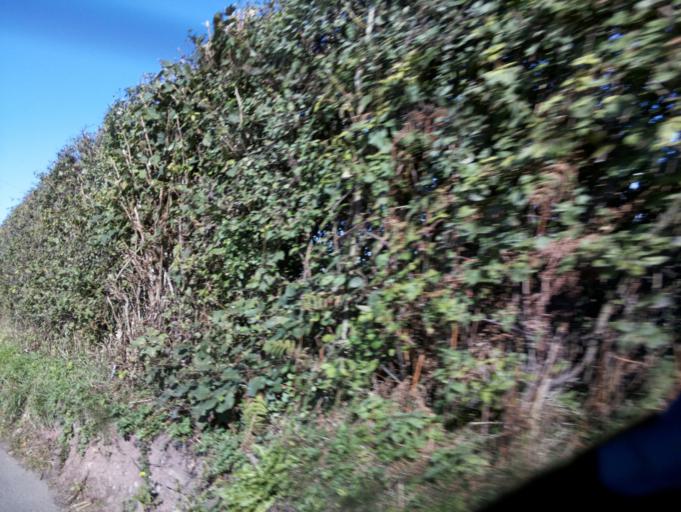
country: GB
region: Wales
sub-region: Caerphilly County Borough
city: Risca
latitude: 51.6094
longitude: -3.0489
